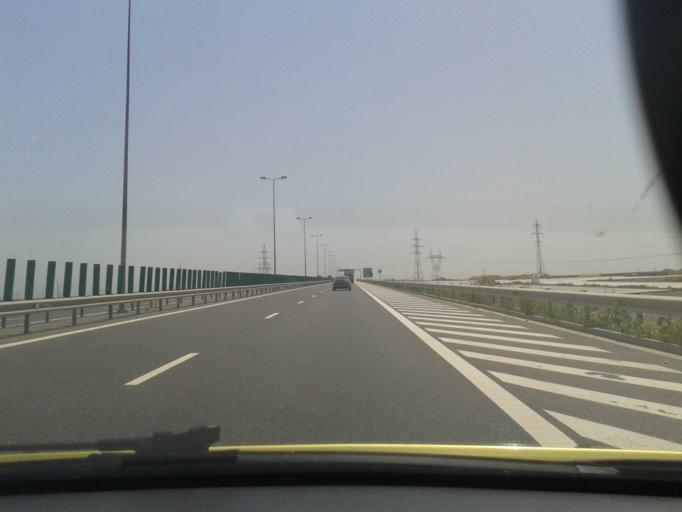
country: RO
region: Constanta
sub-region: Comuna Ovidiu
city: Ovidiu
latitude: 44.2324
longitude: 28.5496
